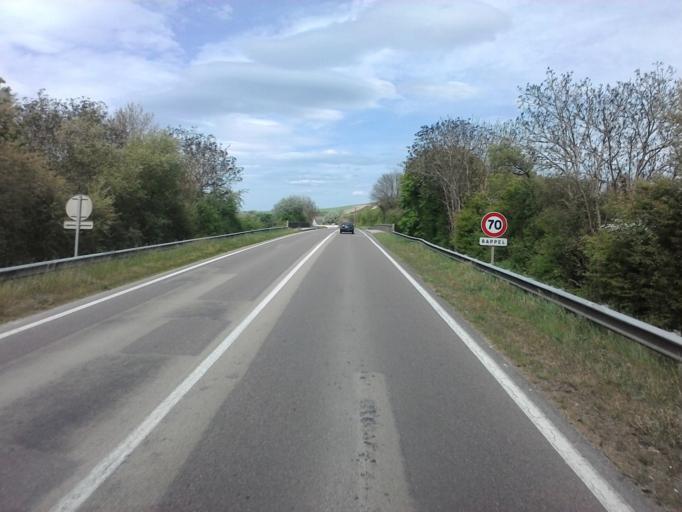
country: FR
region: Bourgogne
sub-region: Departement de l'Yonne
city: Champs-sur-Yonne
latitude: 47.7352
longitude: 3.6052
